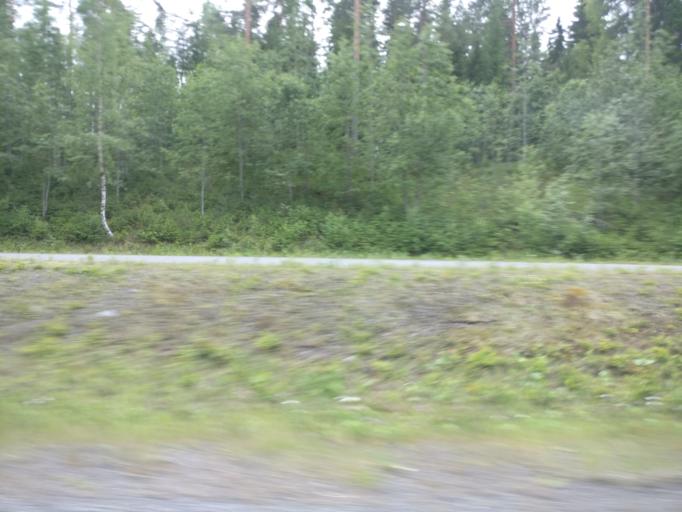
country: FI
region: Northern Savo
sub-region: Kuopio
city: Vehmersalmi
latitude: 62.9409
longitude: 27.9065
